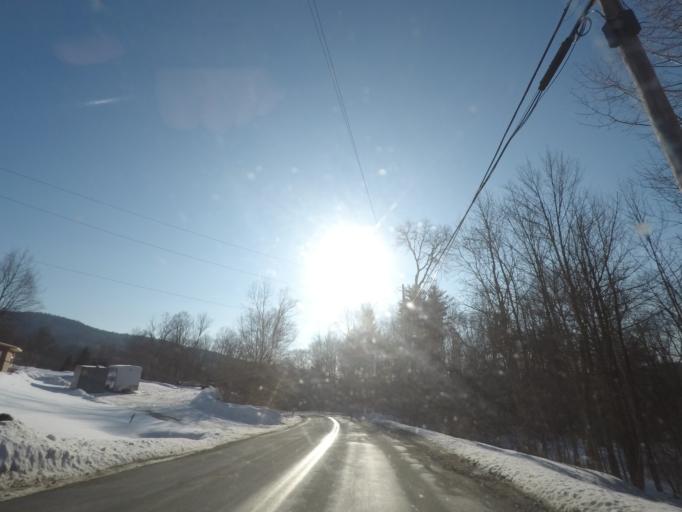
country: US
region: Massachusetts
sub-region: Berkshire County
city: Richmond
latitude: 42.5160
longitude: -73.4196
